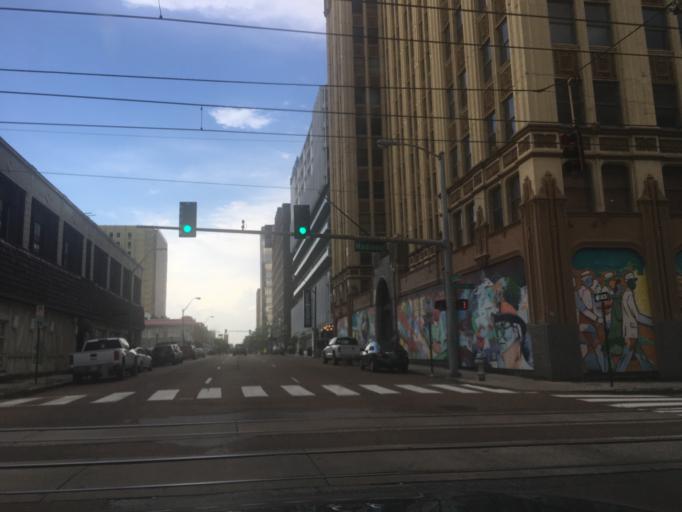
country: US
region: Tennessee
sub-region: Shelby County
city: Memphis
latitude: 35.1444
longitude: -90.0504
